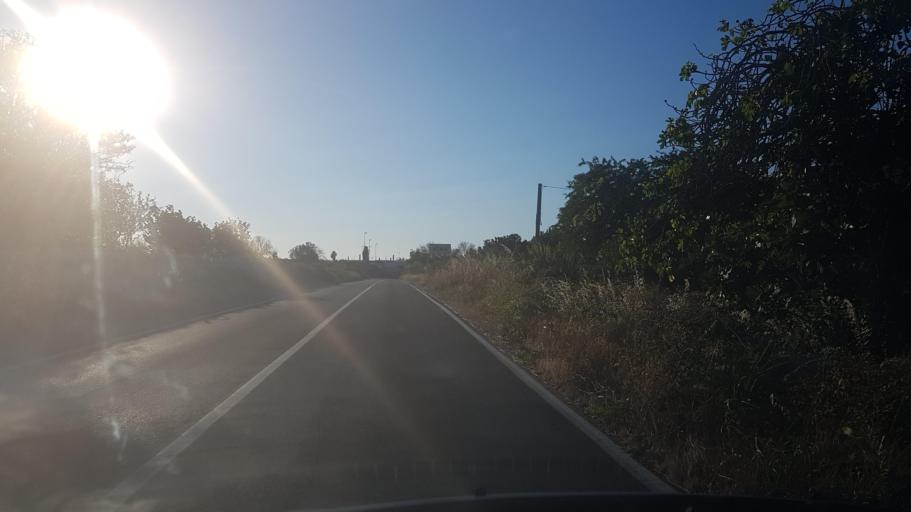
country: IT
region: Apulia
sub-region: Provincia di Lecce
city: Struda
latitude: 40.3311
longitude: 18.2993
